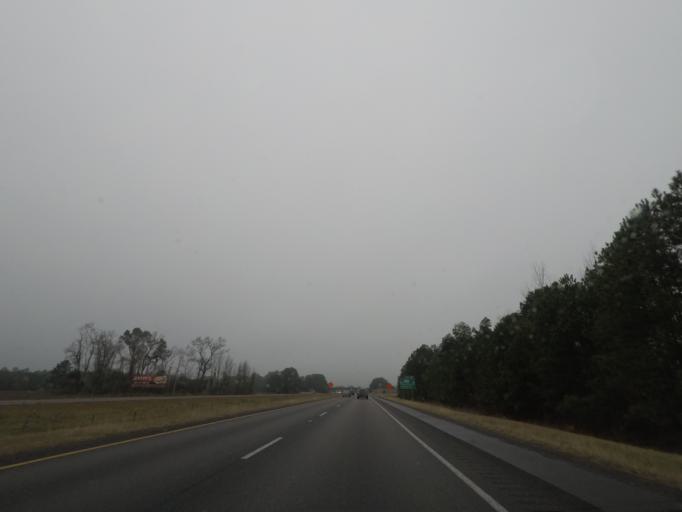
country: US
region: South Carolina
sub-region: Sumter County
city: East Sumter
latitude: 33.8649
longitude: -80.1100
